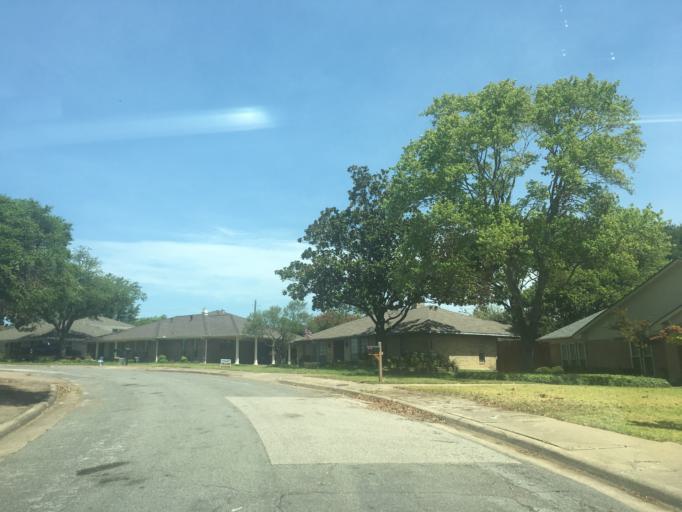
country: US
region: Texas
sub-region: Dallas County
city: University Park
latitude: 32.8777
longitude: -96.7358
